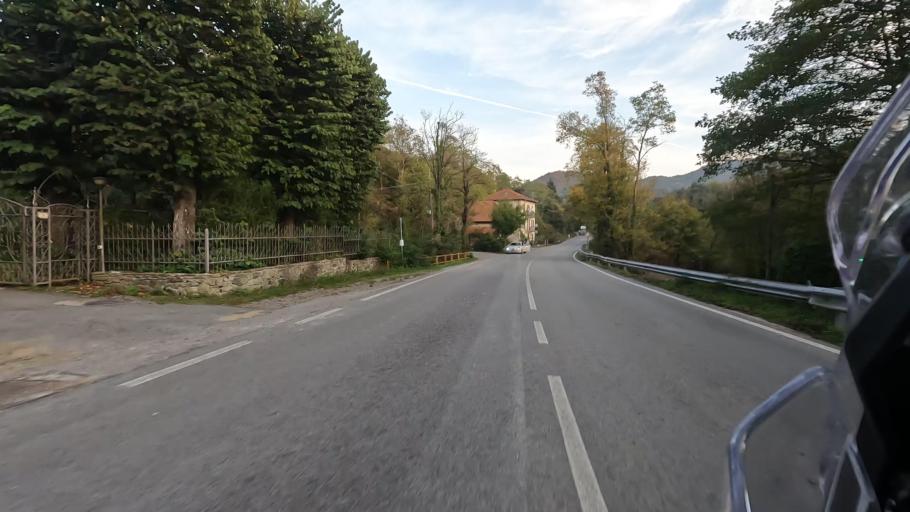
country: IT
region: Liguria
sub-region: Provincia di Savona
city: Osteria dei Cacciatori-Stella
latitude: 44.4344
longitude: 8.4538
